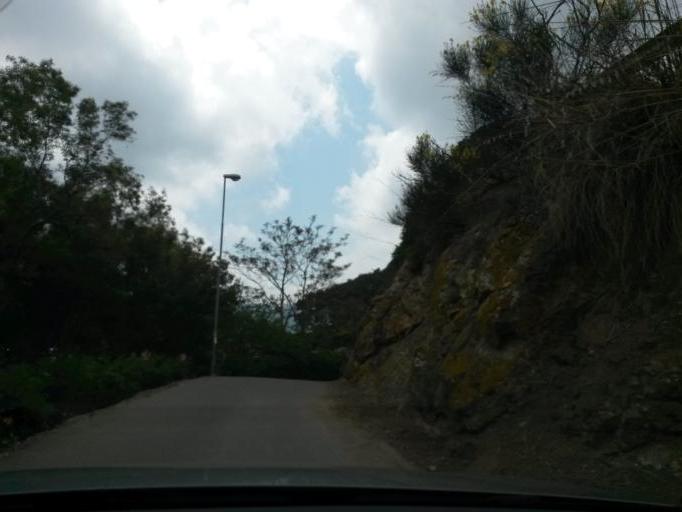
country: IT
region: Tuscany
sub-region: Provincia di Livorno
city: Porto Azzurro
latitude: 42.7703
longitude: 10.4062
